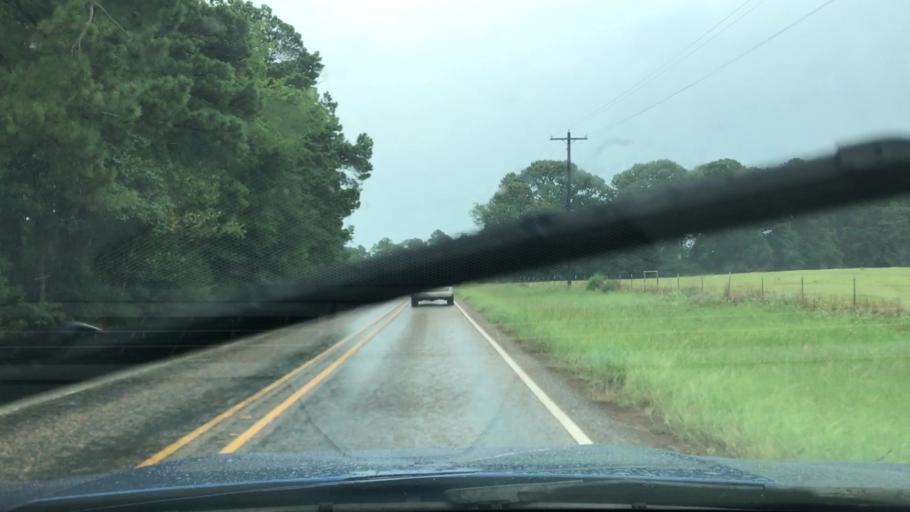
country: US
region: Texas
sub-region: Harrison County
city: Waskom
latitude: 32.4837
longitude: -94.1158
